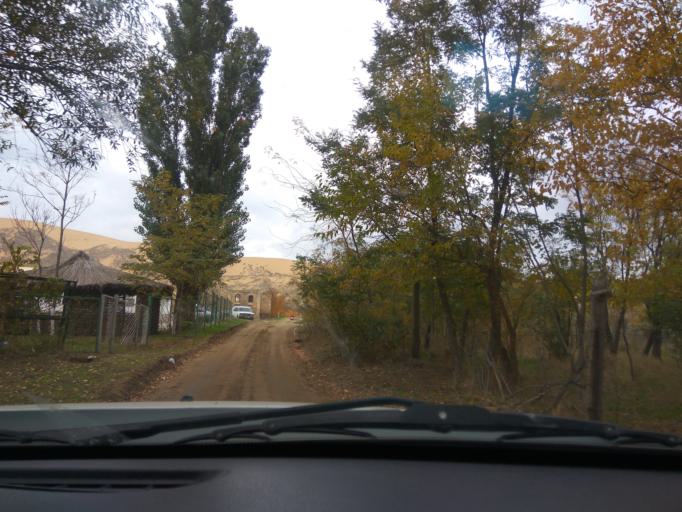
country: RU
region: Dagestan
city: Korkmaskala
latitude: 43.0023
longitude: 47.2386
